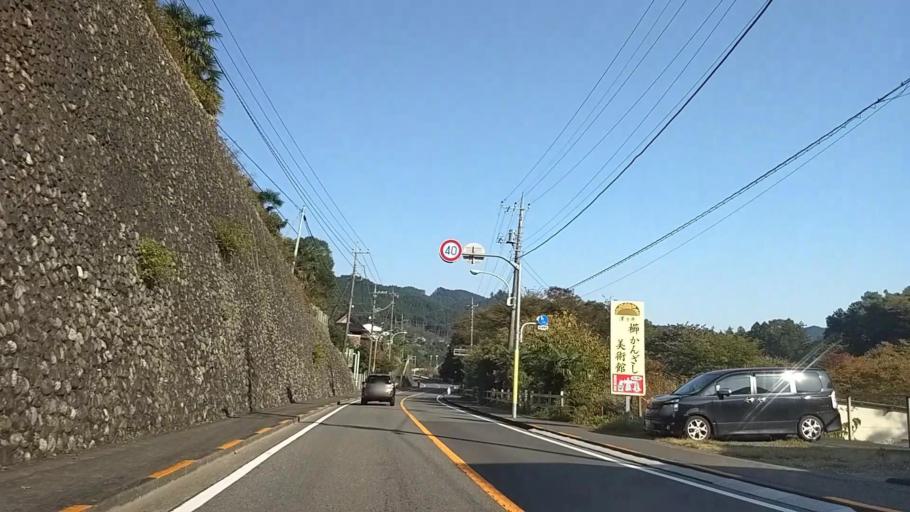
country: JP
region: Tokyo
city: Ome
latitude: 35.8053
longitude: 139.2045
